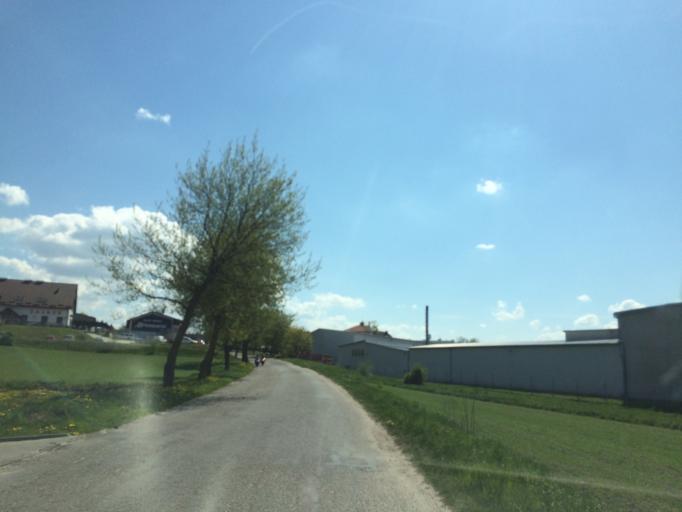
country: PL
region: Warmian-Masurian Voivodeship
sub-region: Powiat ilawski
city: Lubawa
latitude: 53.5115
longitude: 19.7448
